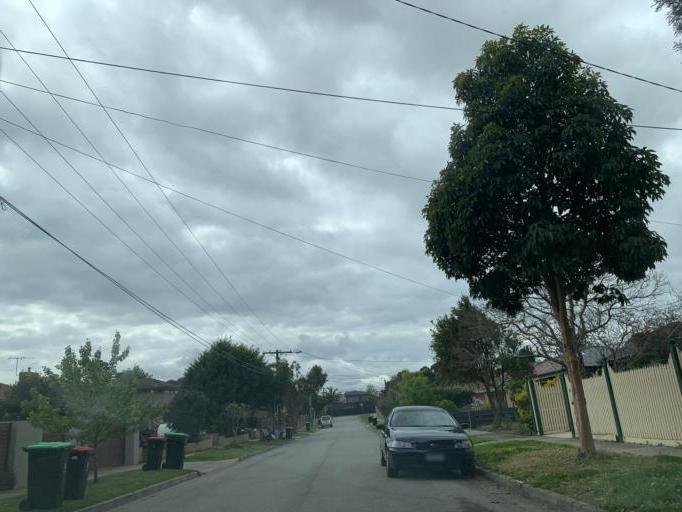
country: AU
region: Victoria
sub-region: Kingston
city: Mentone
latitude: -37.9681
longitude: 145.0669
